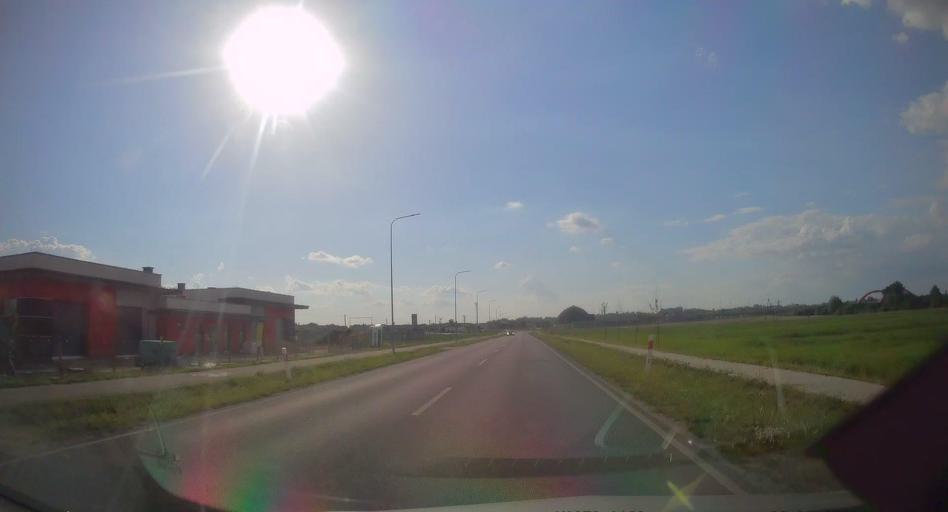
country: PL
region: Subcarpathian Voivodeship
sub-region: Powiat debicki
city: Zyrakow
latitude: 50.0743
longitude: 21.3879
